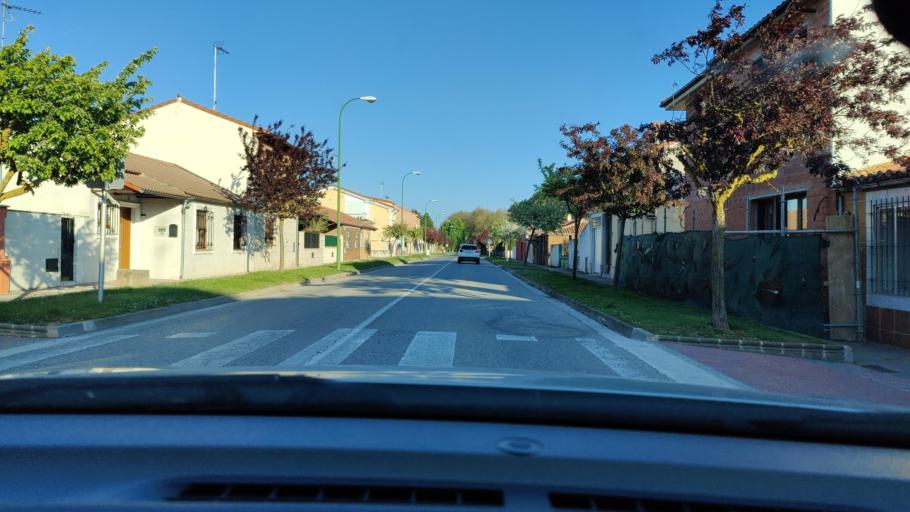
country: ES
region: Castille and Leon
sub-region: Provincia de Burgos
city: Villagonzalo-Pedernales
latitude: 42.3481
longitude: -3.7323
